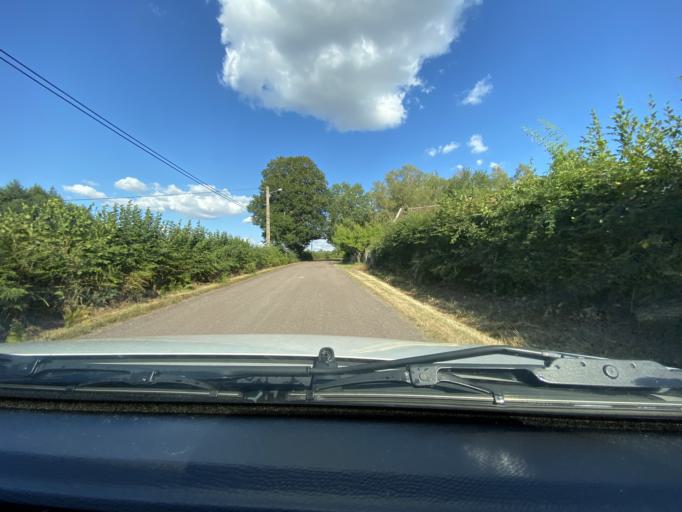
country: FR
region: Bourgogne
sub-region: Departement de la Cote-d'Or
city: Saulieu
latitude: 47.3107
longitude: 4.2004
